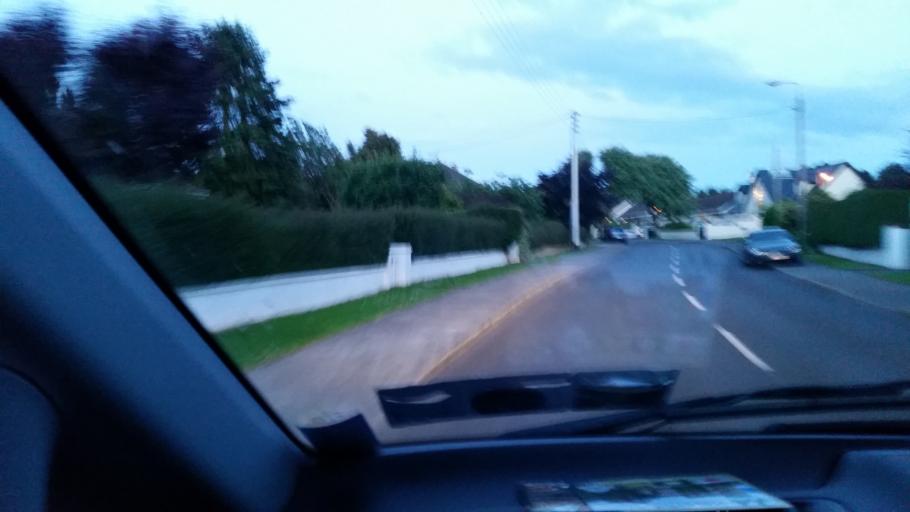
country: IE
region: Leinster
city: Foxrock
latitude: 53.2645
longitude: -6.1769
